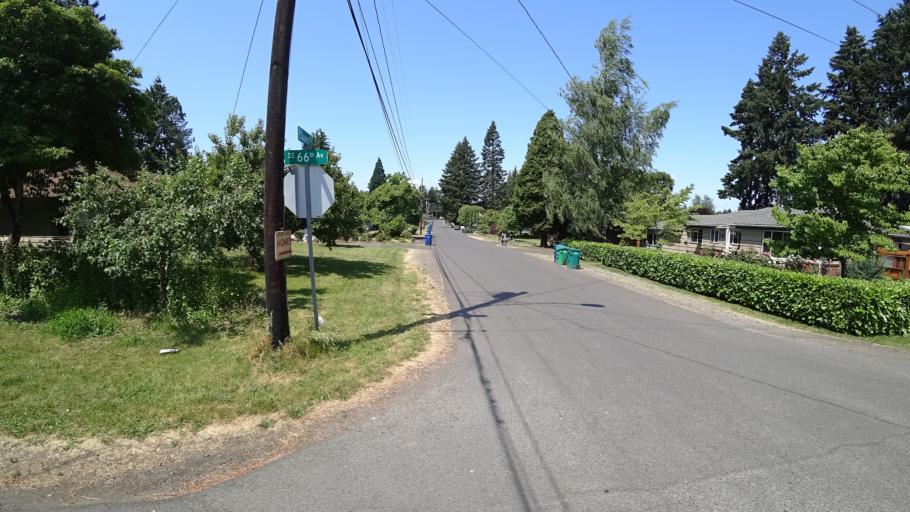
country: US
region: Oregon
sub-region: Clackamas County
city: Oatfield
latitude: 45.4468
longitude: -122.5952
